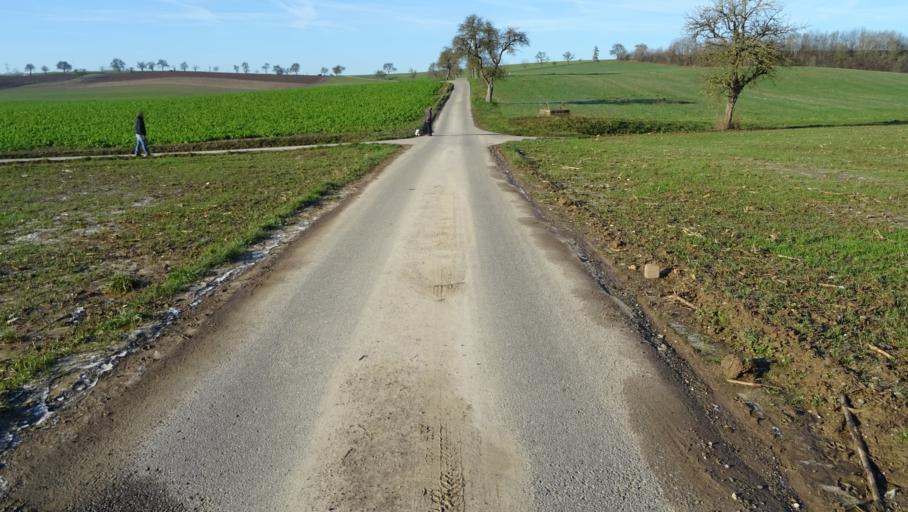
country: DE
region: Baden-Wuerttemberg
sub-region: Karlsruhe Region
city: Mosbach
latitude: 49.3515
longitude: 9.1856
